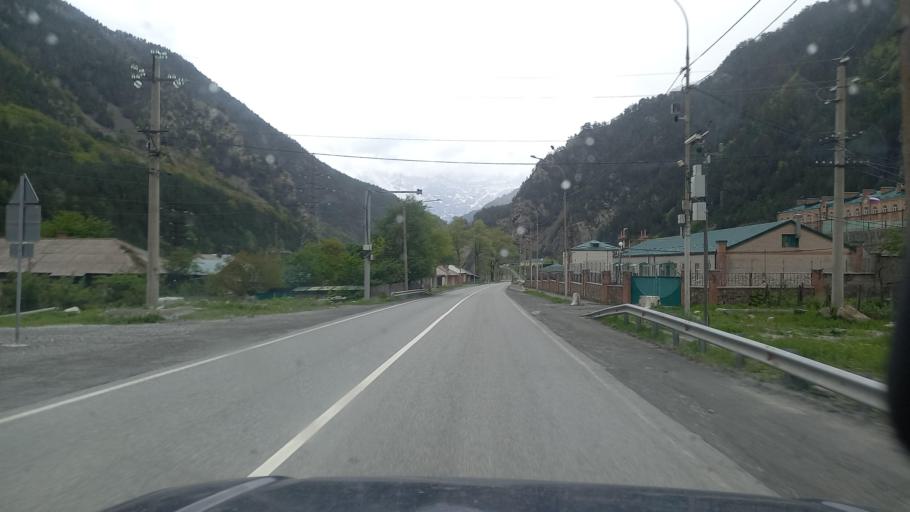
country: RU
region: North Ossetia
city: Mizur
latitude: 42.7956
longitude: 44.0072
